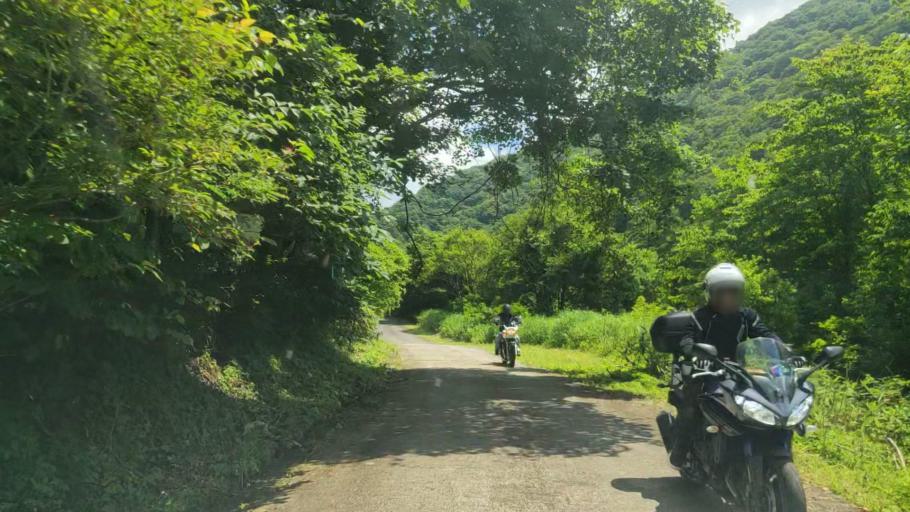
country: JP
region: Fukui
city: Ono
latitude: 35.7890
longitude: 136.5050
